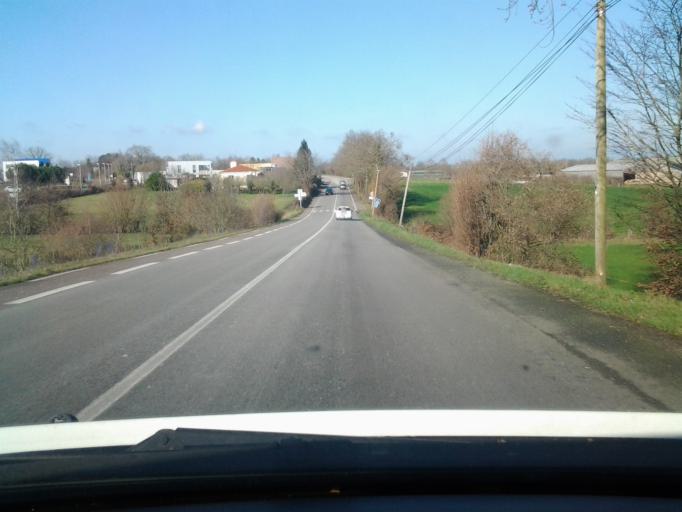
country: FR
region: Pays de la Loire
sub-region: Departement de la Vendee
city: La Roche-sur-Yon
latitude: 46.6863
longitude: -1.4241
